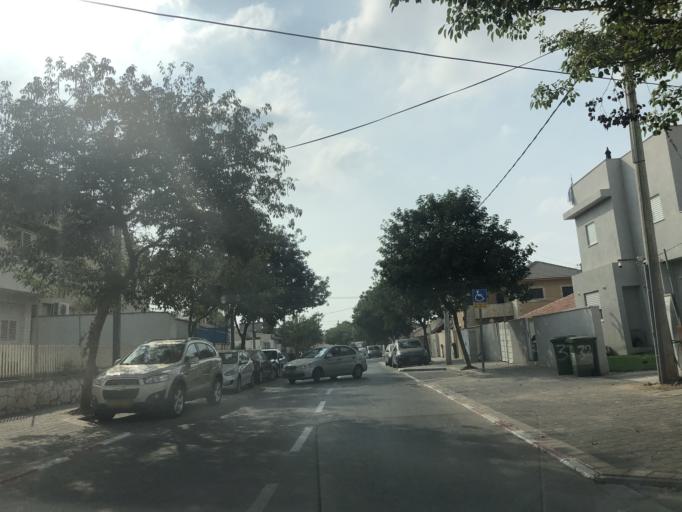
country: IL
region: Central District
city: Rosh Ha'Ayin
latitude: 32.0991
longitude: 34.9519
